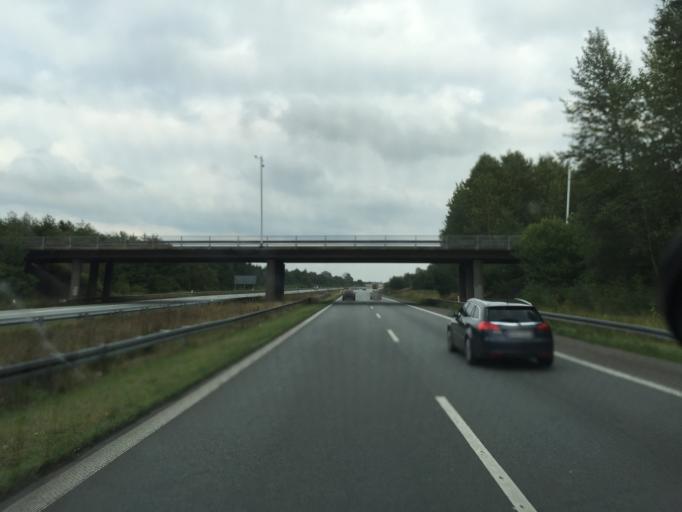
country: DK
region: Zealand
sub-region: Ringsted Kommune
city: Ringsted
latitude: 55.4552
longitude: 11.8244
